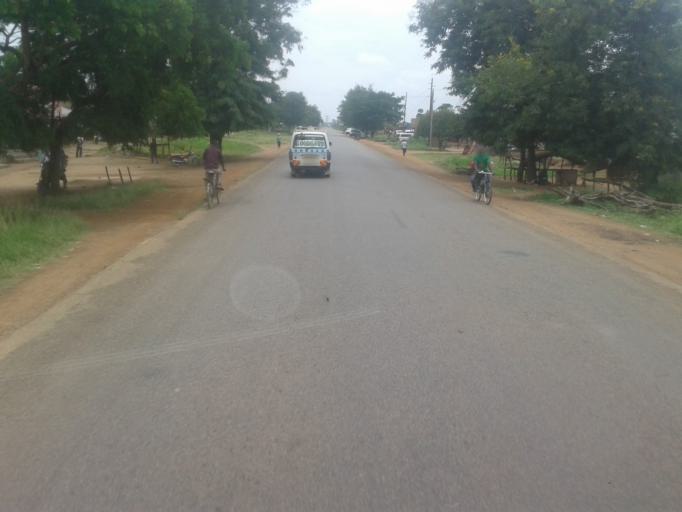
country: UG
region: Western Region
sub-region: Kiryandongo District
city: Masindi Port
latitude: 1.5323
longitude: 32.0427
